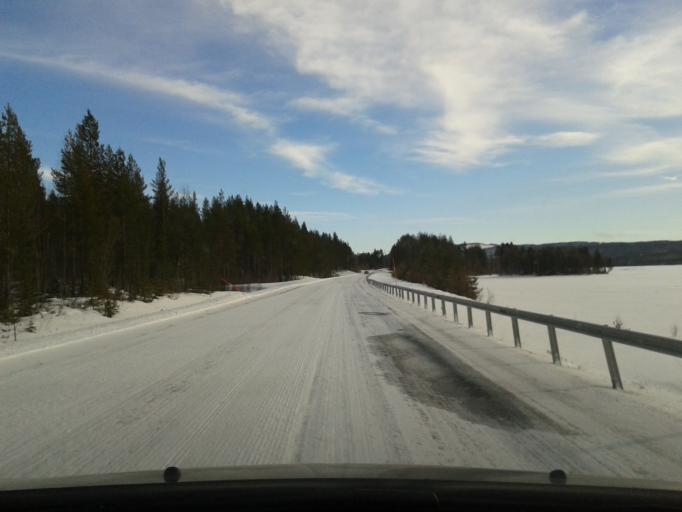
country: SE
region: Vaesterbotten
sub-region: Asele Kommun
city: Asele
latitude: 64.3485
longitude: 16.9953
